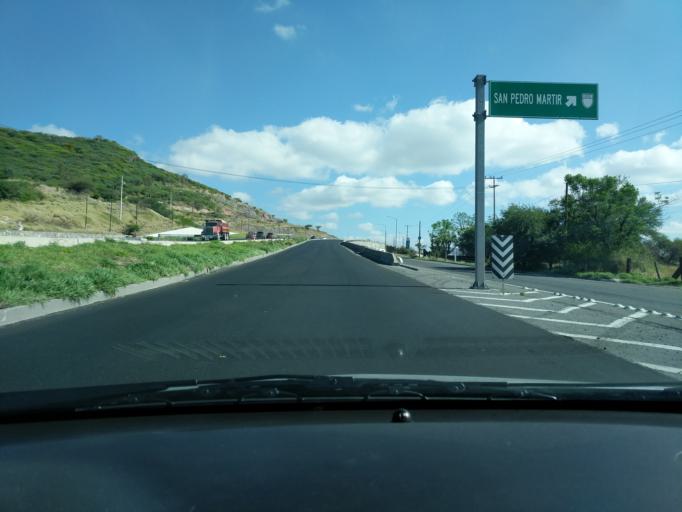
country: MX
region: Guanajuato
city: El Castillo
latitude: 20.6023
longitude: -100.4912
